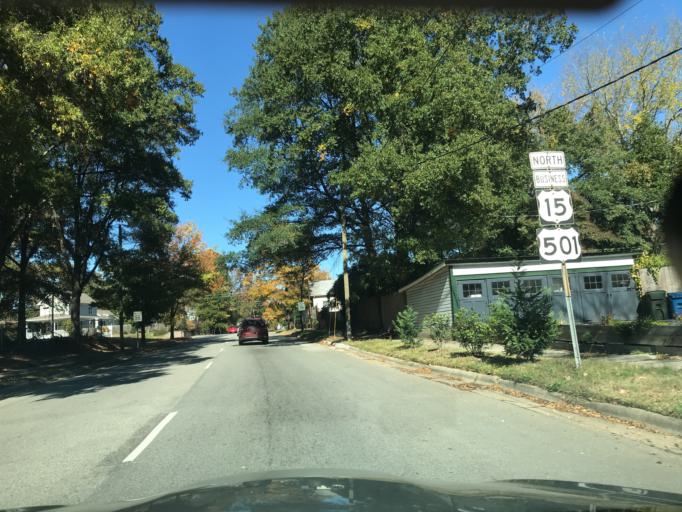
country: US
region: North Carolina
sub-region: Durham County
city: Durham
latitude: 36.0054
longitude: -78.8926
